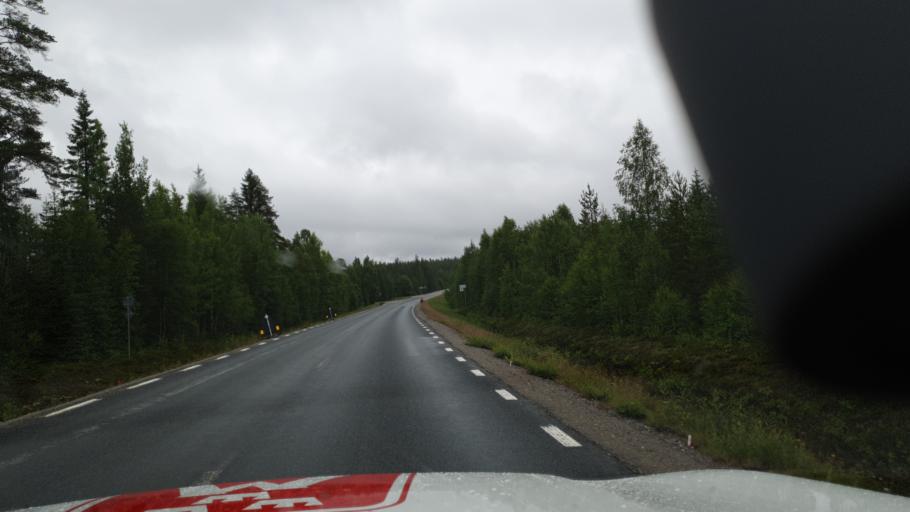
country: SE
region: Vaesterbotten
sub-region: Vannas Kommun
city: Vaennaes
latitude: 63.7841
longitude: 19.7421
